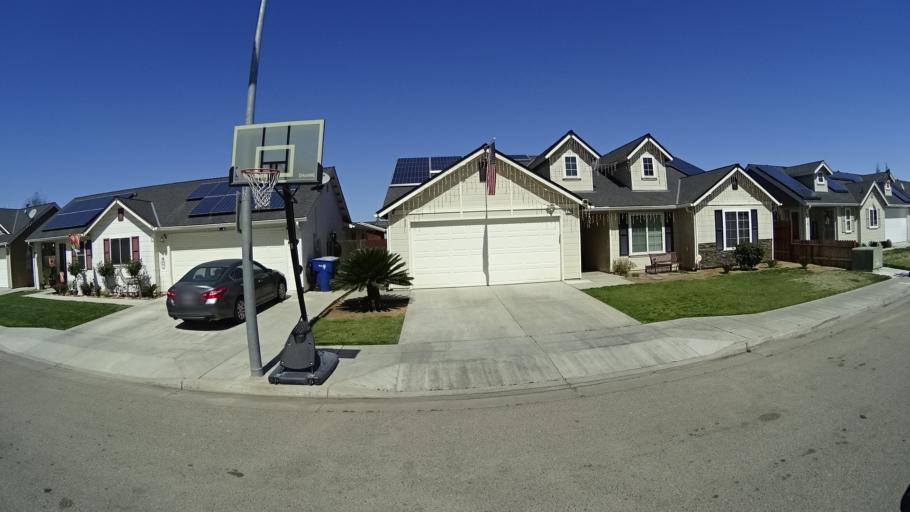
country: US
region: California
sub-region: Fresno County
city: West Park
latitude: 36.7754
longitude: -119.8837
